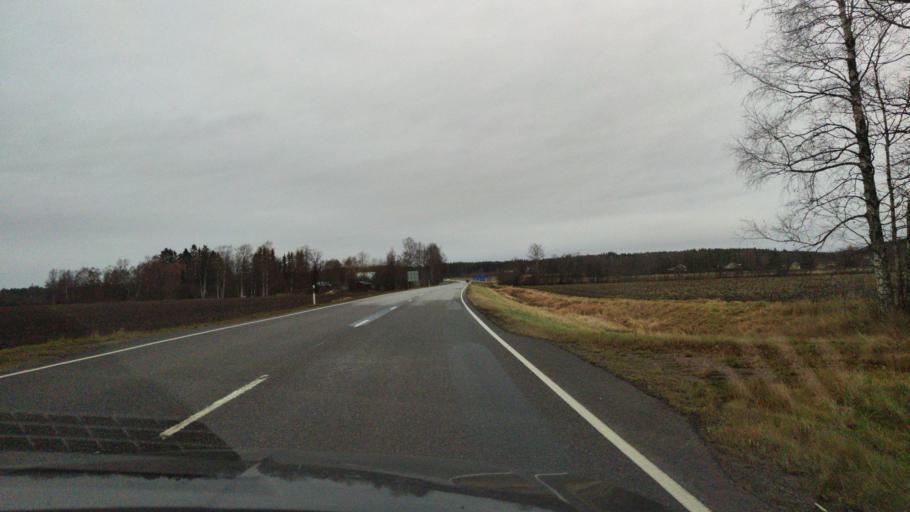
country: FI
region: Varsinais-Suomi
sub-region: Loimaa
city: Ylaene
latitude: 60.8798
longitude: 22.3959
